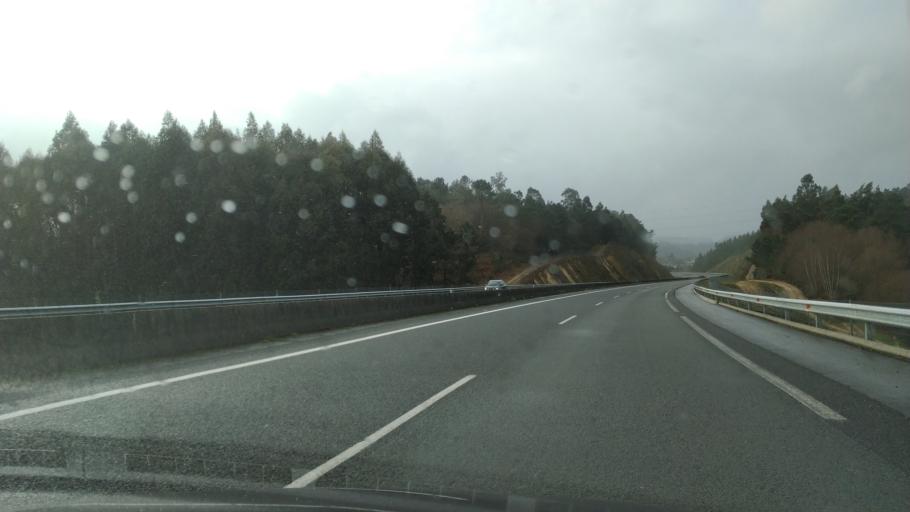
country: ES
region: Galicia
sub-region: Provincia de Pontevedra
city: Silleda
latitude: 42.7187
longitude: -8.2703
